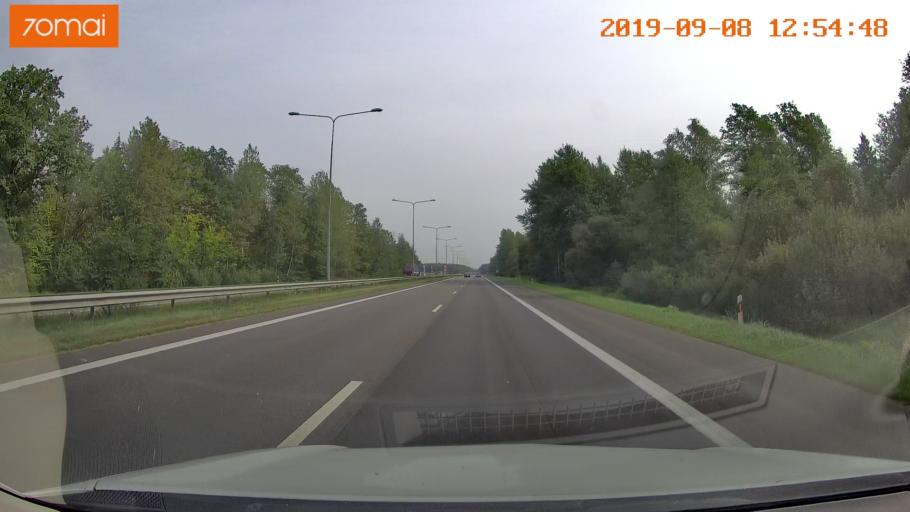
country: LT
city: Ramuciai
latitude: 54.9288
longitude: 24.0277
